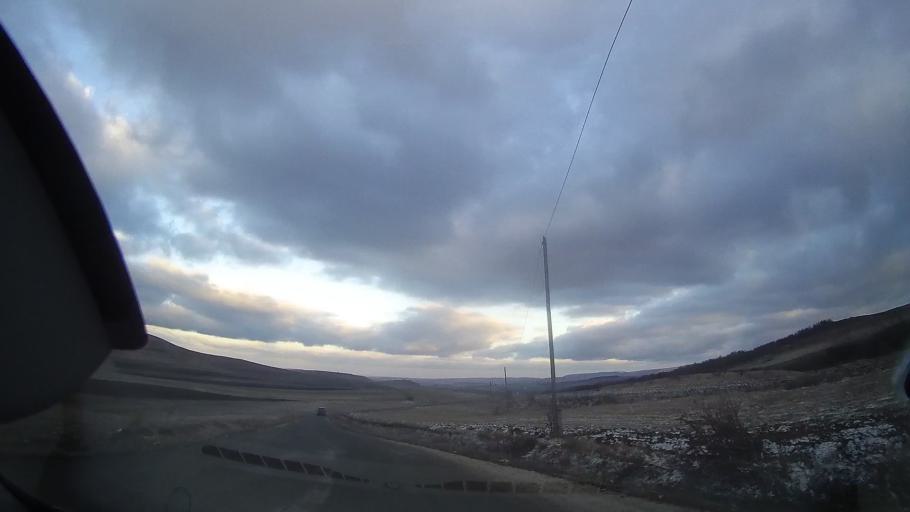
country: RO
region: Cluj
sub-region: Comuna Manastireni
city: Manastireni
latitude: 46.7779
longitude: 23.0567
